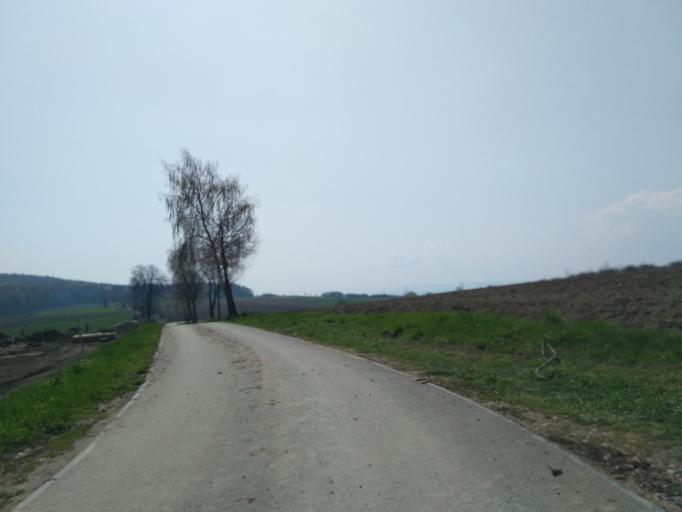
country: PL
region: Subcarpathian Voivodeship
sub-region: Powiat brzozowski
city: Turze Pole
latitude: 49.6412
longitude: 22.0032
